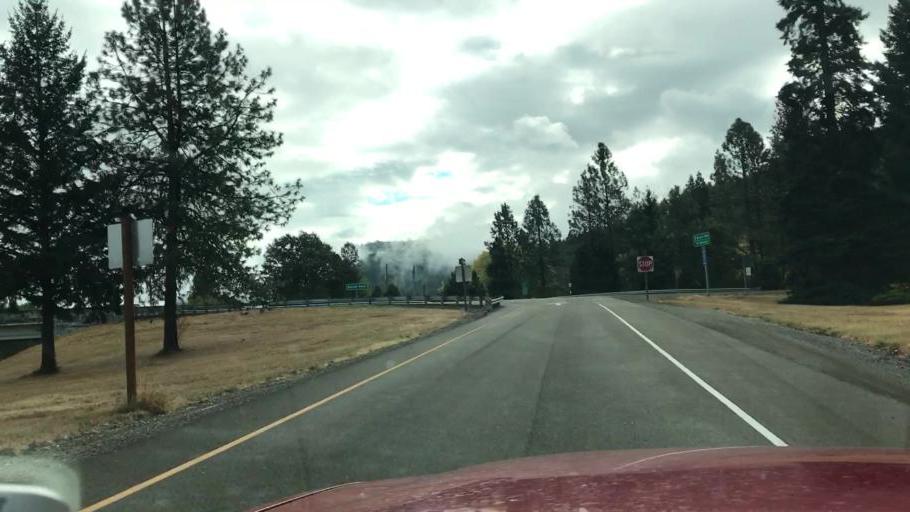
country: US
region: Oregon
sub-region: Douglas County
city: Canyonville
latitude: 42.7661
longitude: -123.3335
